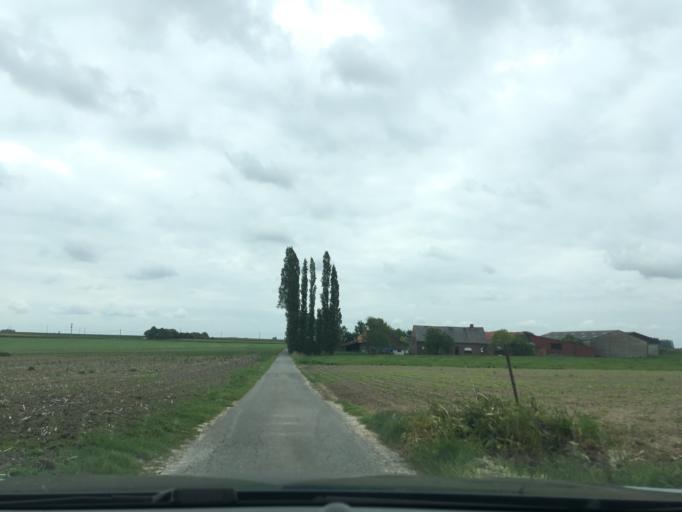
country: BE
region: Flanders
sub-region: Provincie West-Vlaanderen
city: Moorslede
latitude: 50.8447
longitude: 3.0731
